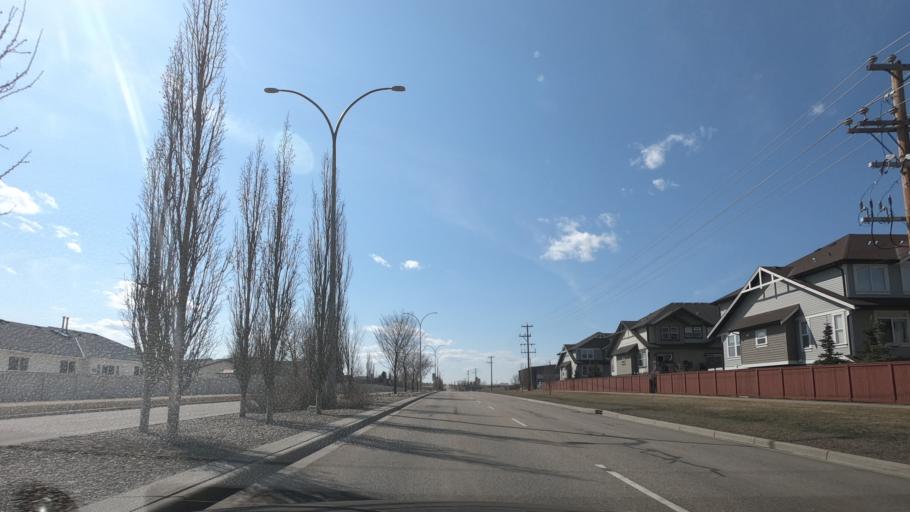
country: CA
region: Alberta
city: Airdrie
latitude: 51.3001
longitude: -114.0346
